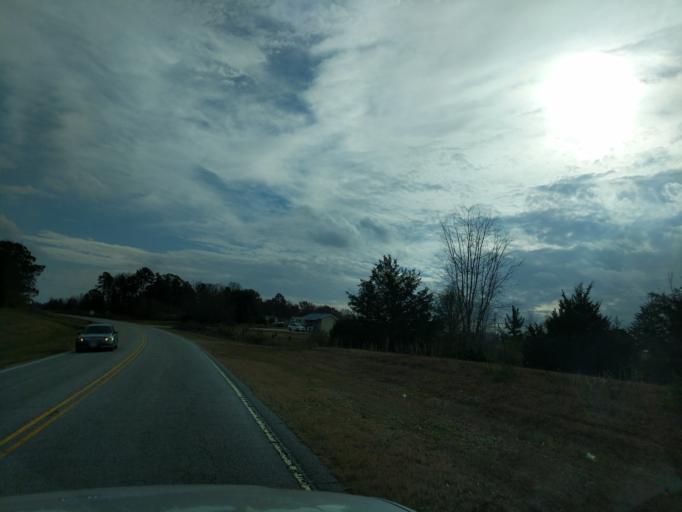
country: US
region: Georgia
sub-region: Franklin County
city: Gumlog
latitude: 34.5583
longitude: -83.0524
